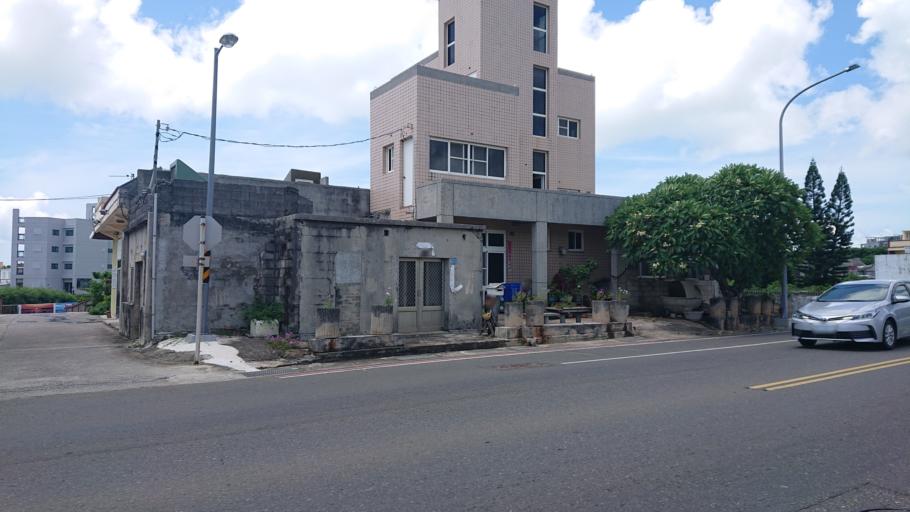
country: TW
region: Taiwan
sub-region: Penghu
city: Ma-kung
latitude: 23.5766
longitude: 119.6029
